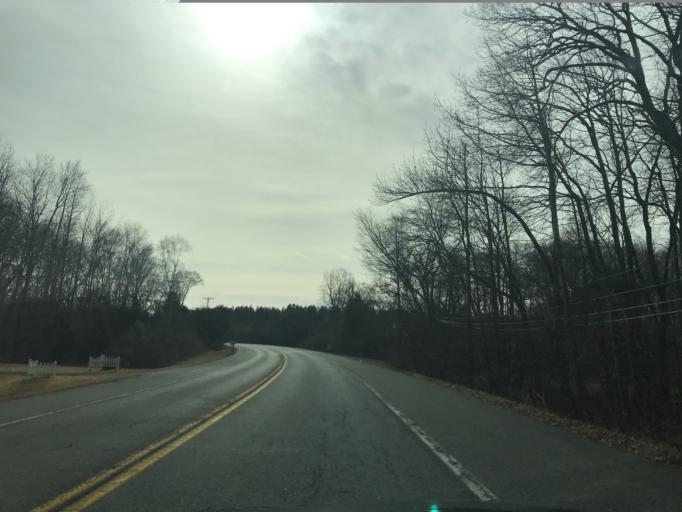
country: US
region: Virginia
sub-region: Prince William County
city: Cherry Hill
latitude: 38.4738
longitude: -77.2254
